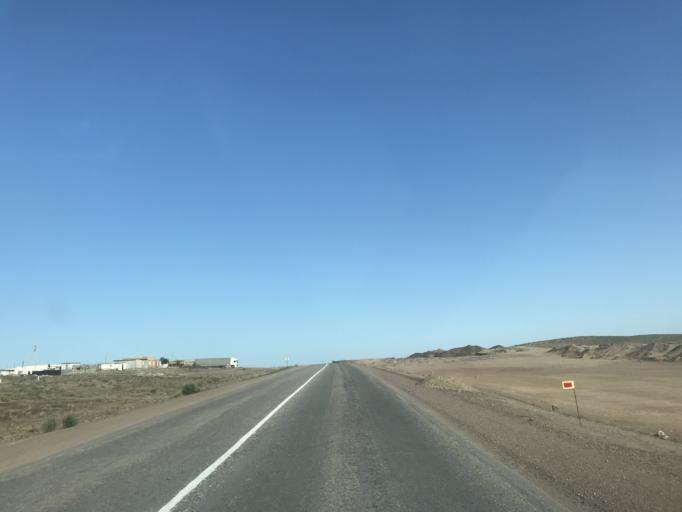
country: KZ
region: Zhambyl
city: Mynaral
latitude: 45.3280
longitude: 73.7307
